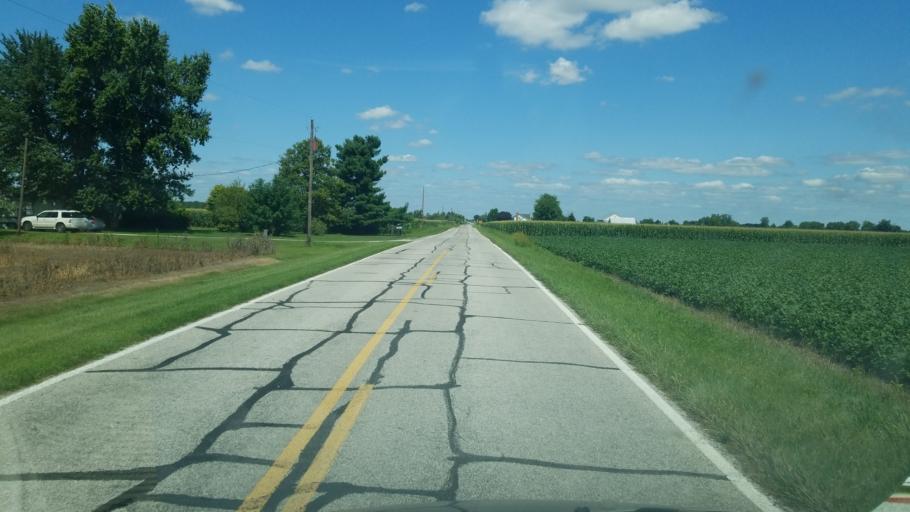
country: US
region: Ohio
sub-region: Fulton County
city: Delta
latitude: 41.6514
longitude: -84.0158
